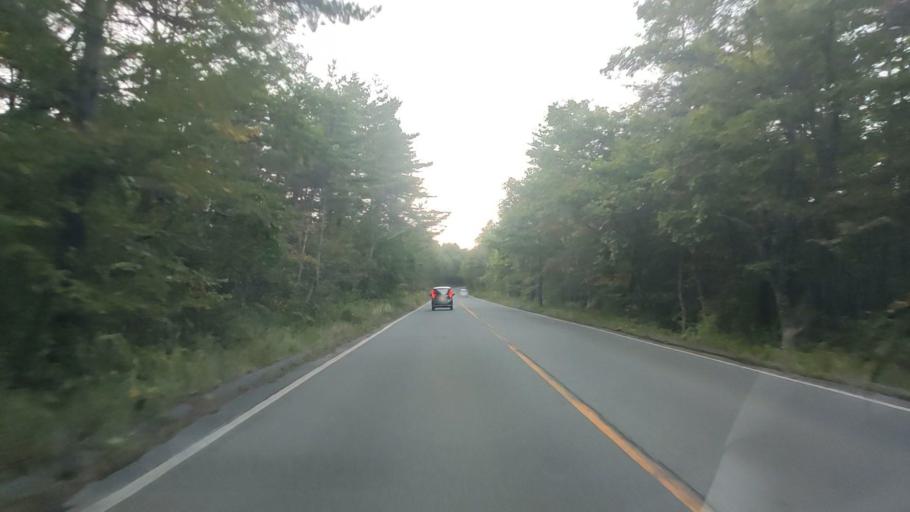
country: JP
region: Nagano
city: Komoro
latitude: 36.4133
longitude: 138.5704
